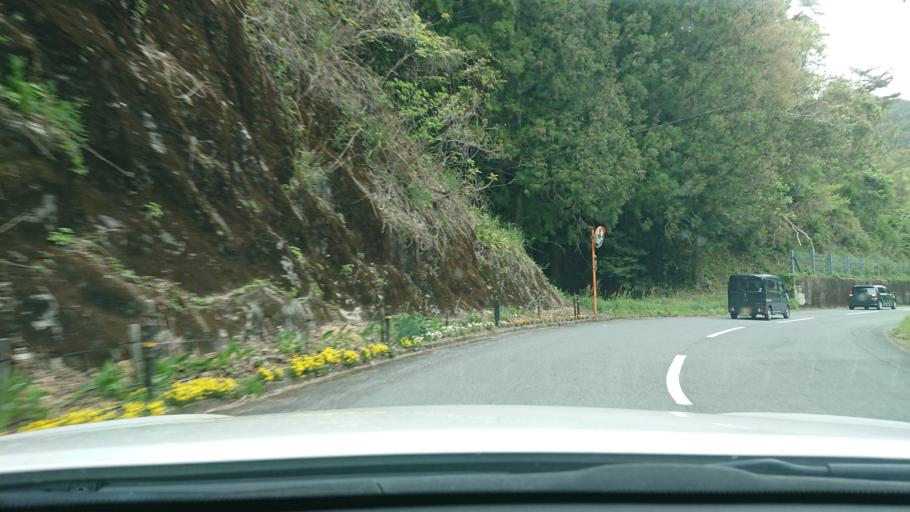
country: JP
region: Tokushima
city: Ishii
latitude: 33.9171
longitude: 134.4244
